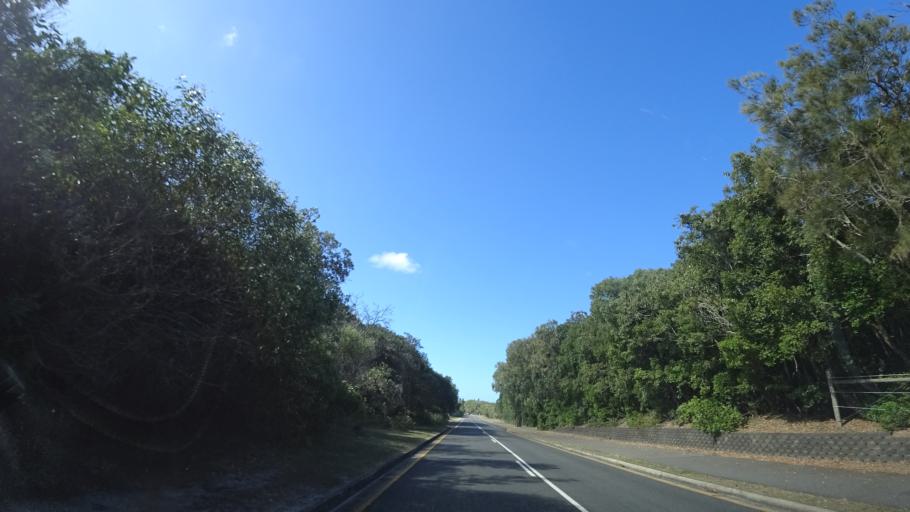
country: AU
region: Queensland
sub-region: Sunshine Coast
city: Mooloolaba
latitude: -26.6199
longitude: 153.1006
